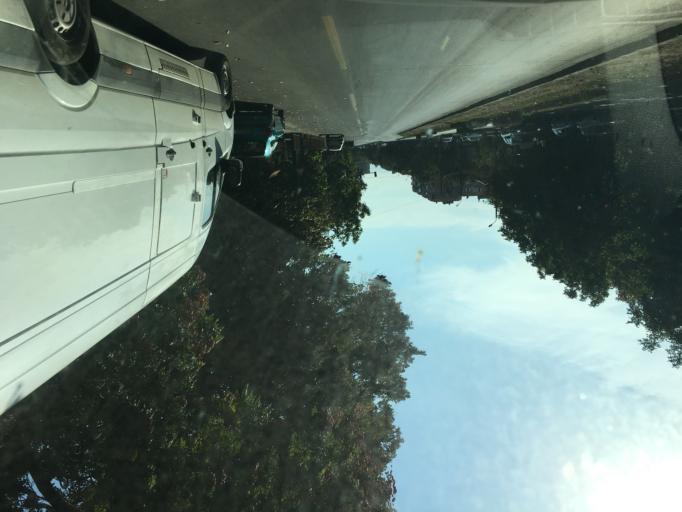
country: BG
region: Pazardzhik
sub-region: Obshtina Pazardzhik
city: Pazardzhik
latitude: 42.2062
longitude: 24.3289
